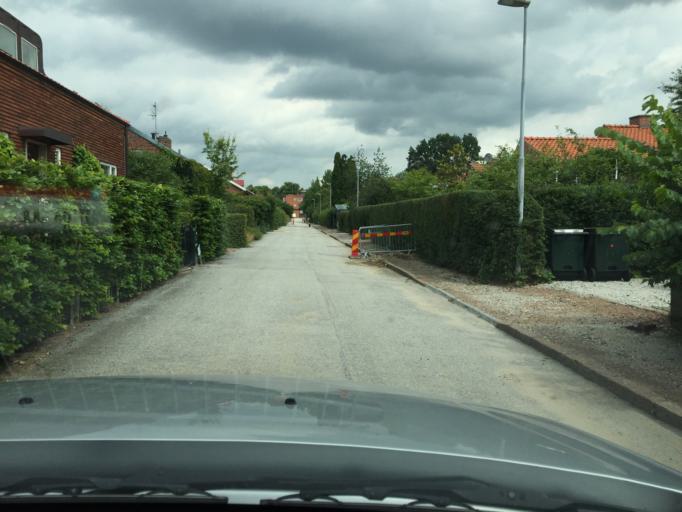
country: SE
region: Skane
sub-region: Lunds Kommun
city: Lund
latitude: 55.6991
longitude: 13.1742
